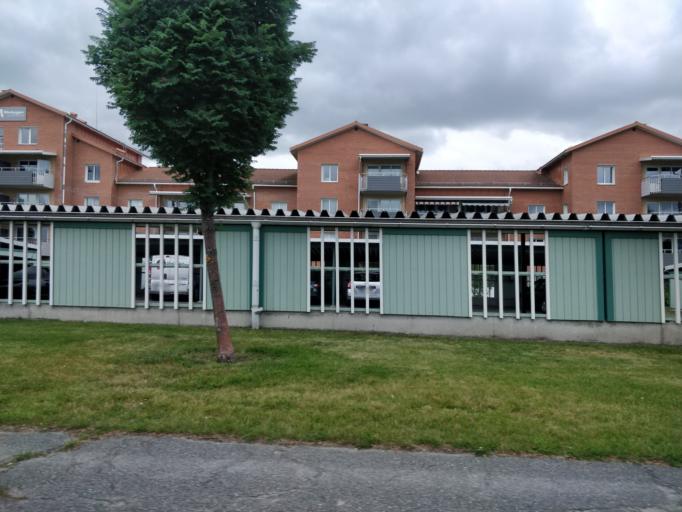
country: SE
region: Vaesterbotten
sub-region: Skelleftea Kommun
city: Viken
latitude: 64.7586
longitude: 20.9016
